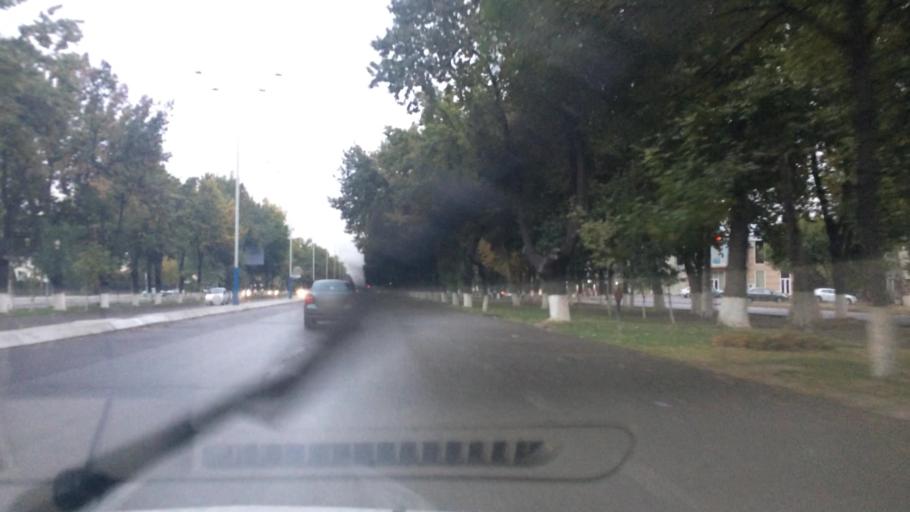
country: UZ
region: Toshkent Shahri
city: Tashkent
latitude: 41.2705
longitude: 69.2020
